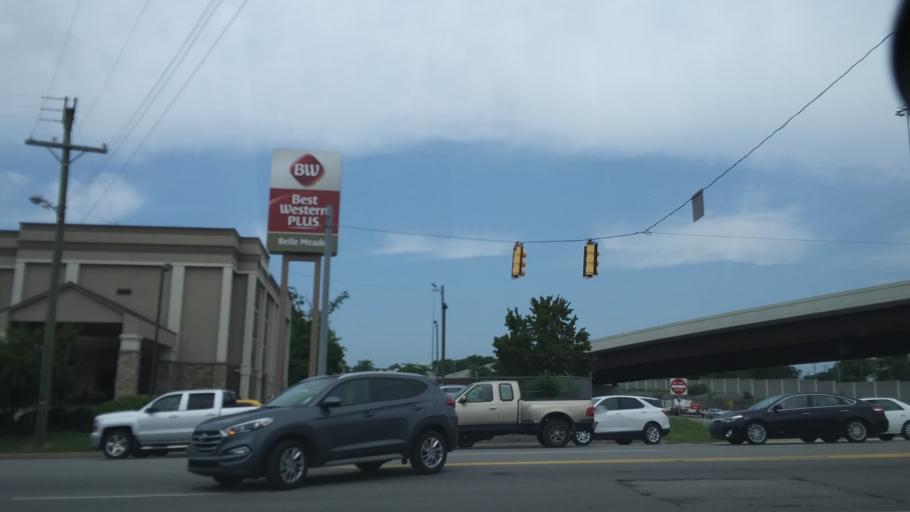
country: US
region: Tennessee
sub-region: Davidson County
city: Belle Meade
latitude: 36.1512
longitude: -86.8571
